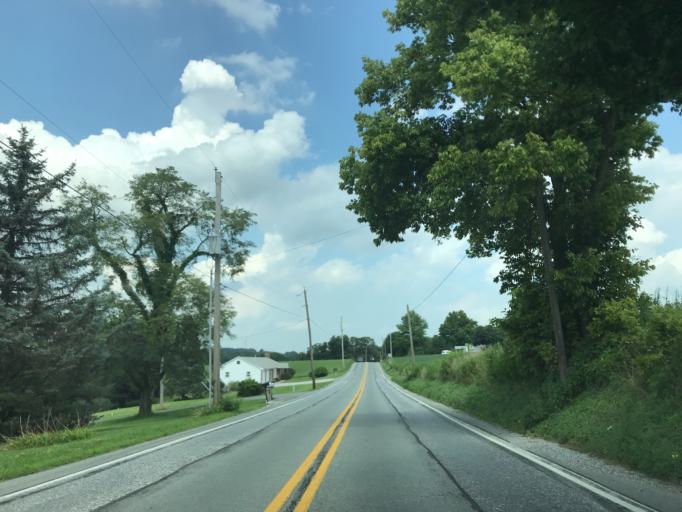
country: US
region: Pennsylvania
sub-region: York County
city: Red Lion
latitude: 39.8785
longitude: -76.6123
